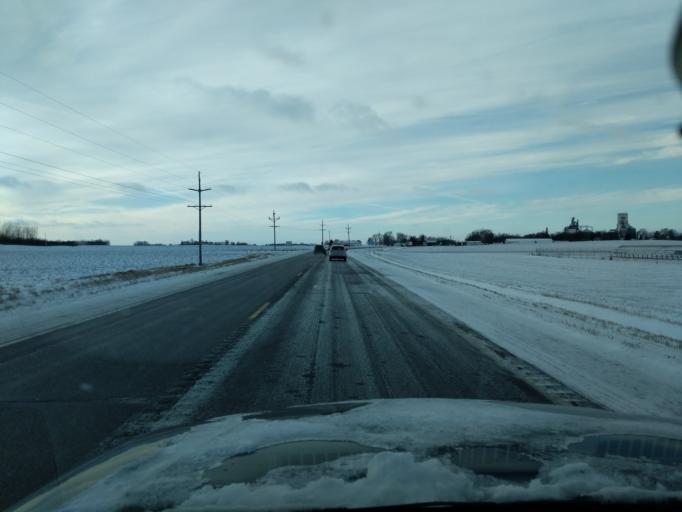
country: US
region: Minnesota
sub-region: Renville County
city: Hector
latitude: 44.7314
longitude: -94.6077
